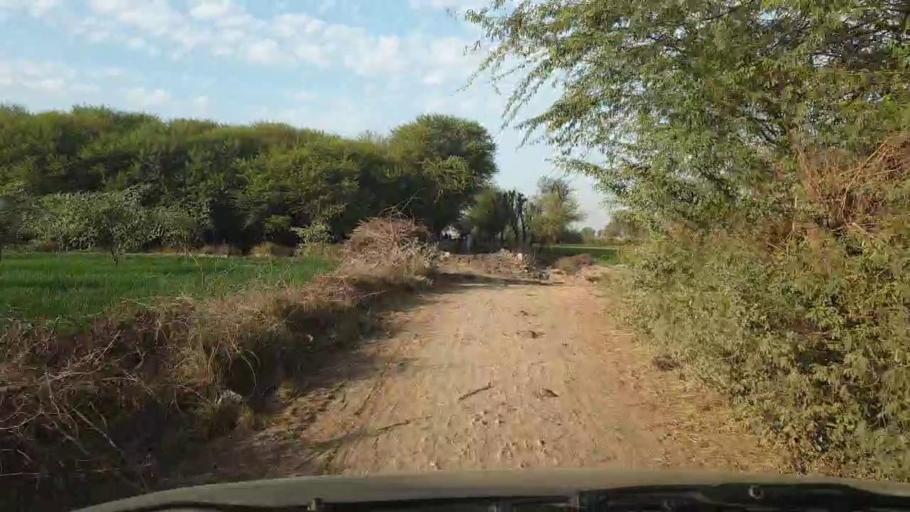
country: PK
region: Sindh
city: Sakrand
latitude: 26.0275
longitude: 68.3684
